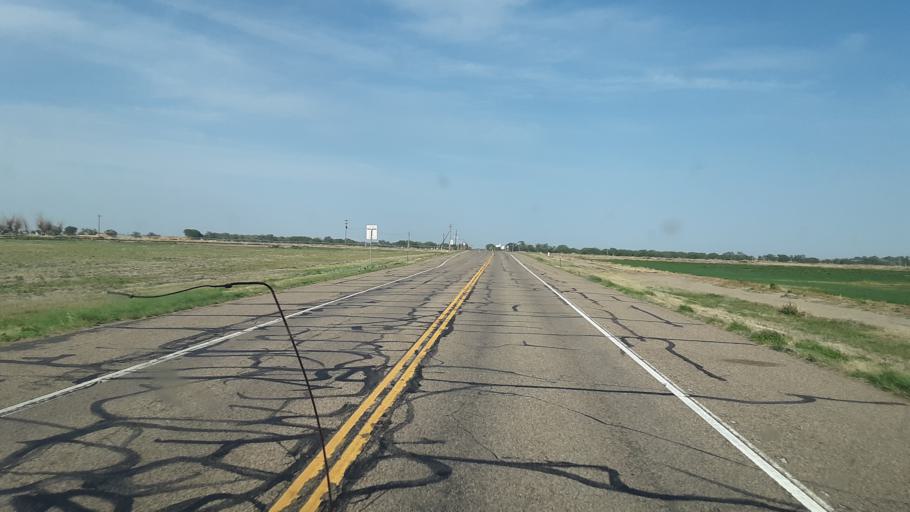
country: US
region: Colorado
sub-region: Prowers County
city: Lamar
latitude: 38.0636
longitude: -102.3500
